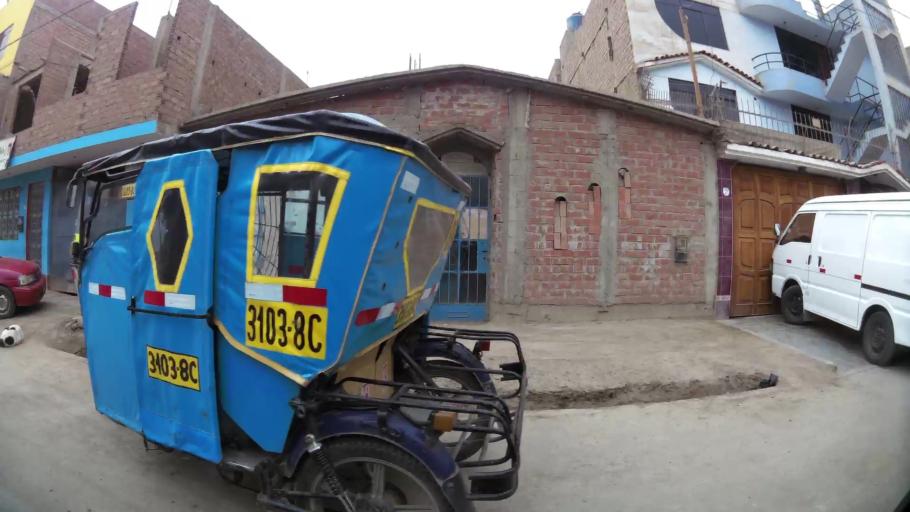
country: PE
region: Lima
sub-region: Lima
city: Independencia
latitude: -11.9684
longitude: -77.0895
